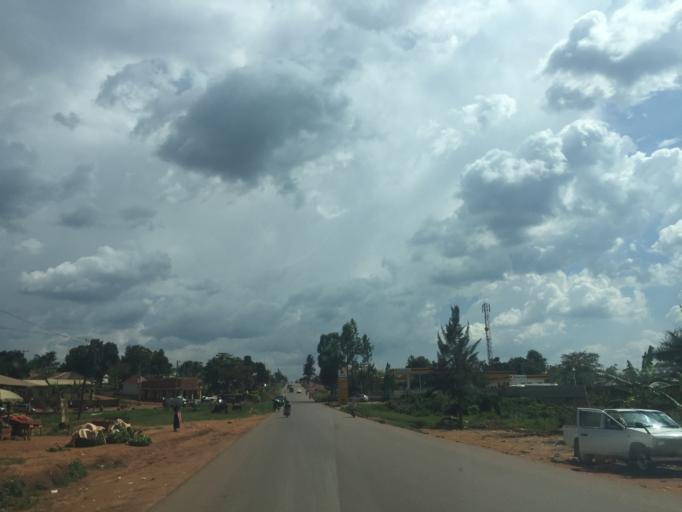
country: UG
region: Central Region
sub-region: Luwero District
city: Wobulenzi
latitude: 0.7238
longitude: 32.5282
